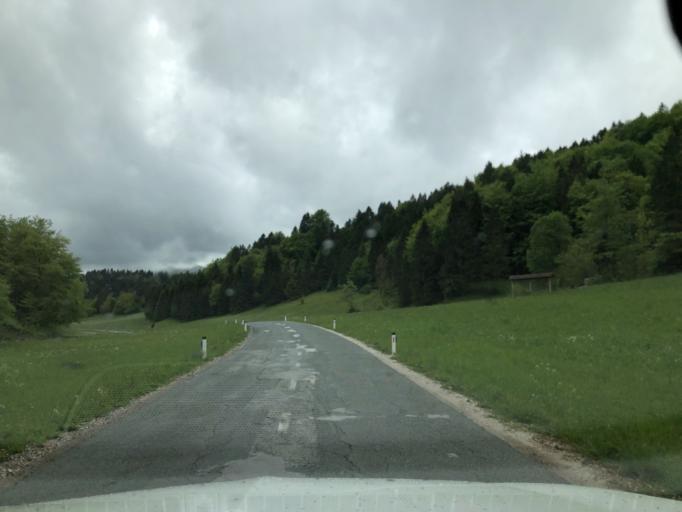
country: SI
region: Gorje
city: Zgornje Gorje
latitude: 46.4003
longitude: 14.0743
